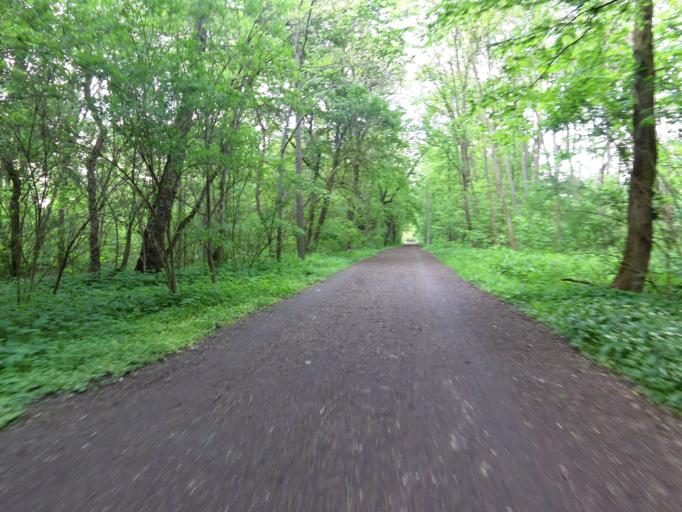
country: DE
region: Saxony
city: Leipzig
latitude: 51.3136
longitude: 12.3372
